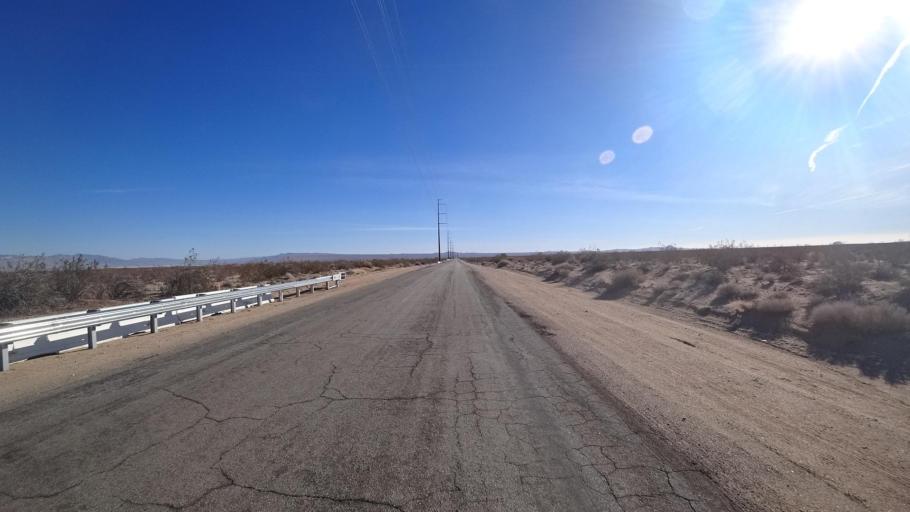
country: US
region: California
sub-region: Kern County
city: California City
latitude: 35.1986
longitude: -118.0426
